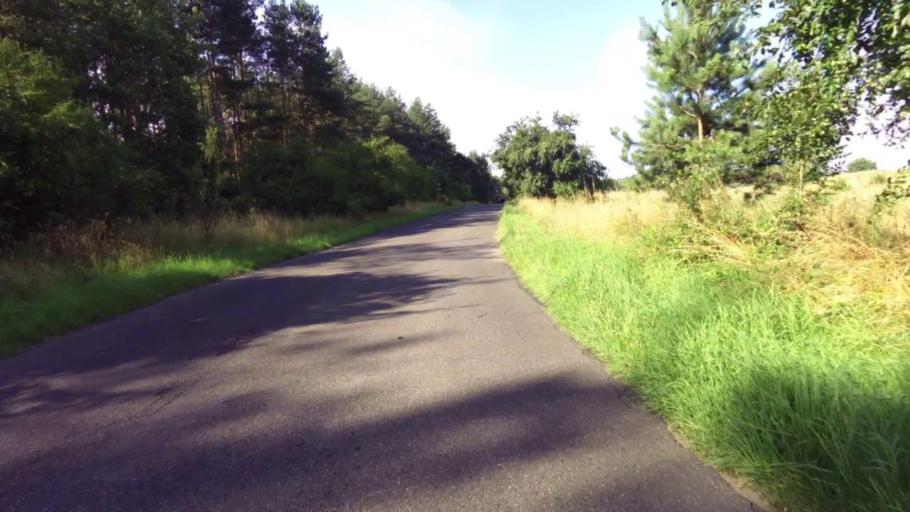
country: PL
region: West Pomeranian Voivodeship
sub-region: Powiat stargardzki
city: Marianowo
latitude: 53.3758
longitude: 15.2618
